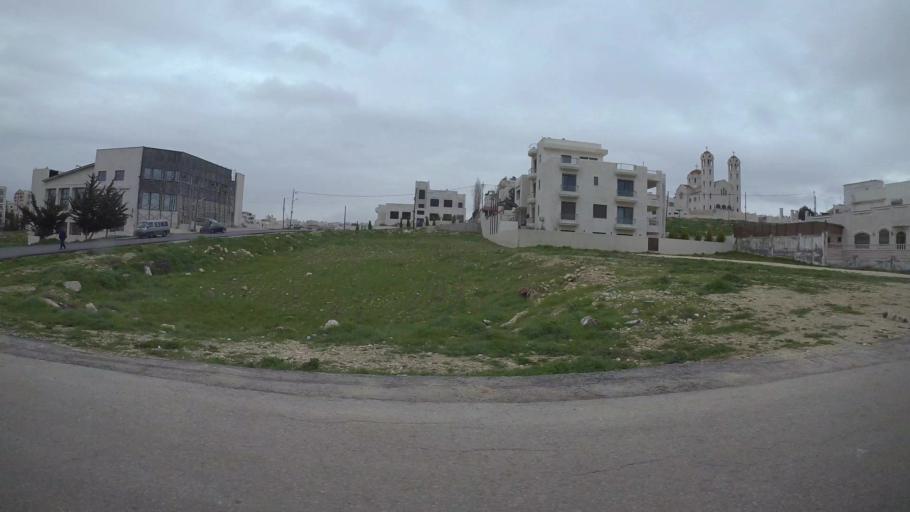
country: JO
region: Amman
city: Al Jubayhah
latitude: 31.9926
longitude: 35.8411
